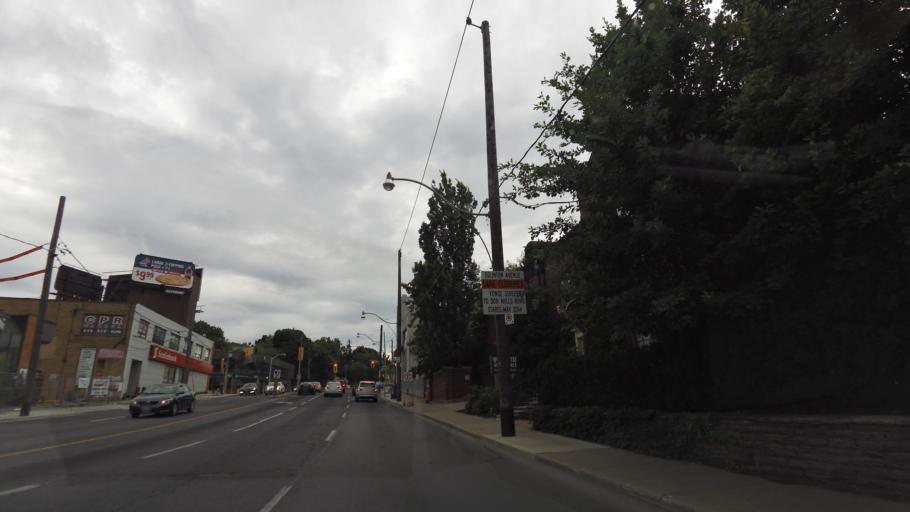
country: CA
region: Ontario
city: Toronto
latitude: 43.7003
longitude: -79.4252
